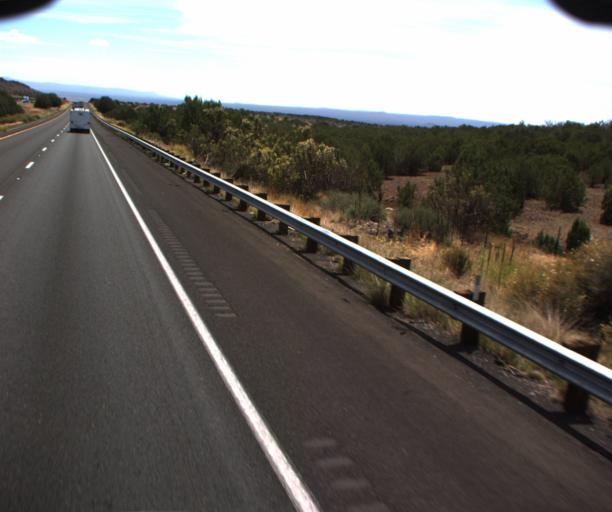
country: US
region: Arizona
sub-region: Yavapai County
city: Paulden
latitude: 35.2531
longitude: -112.6992
